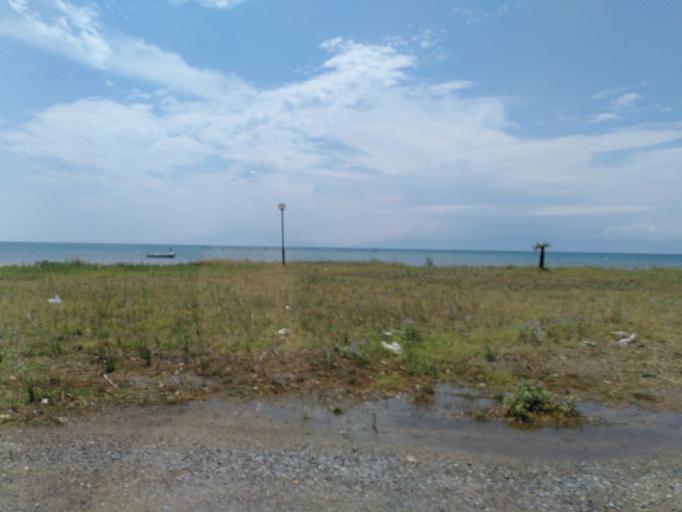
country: GR
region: Central Macedonia
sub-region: Nomos Thessalonikis
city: Nea Michaniona
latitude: 40.4305
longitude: 22.8717
